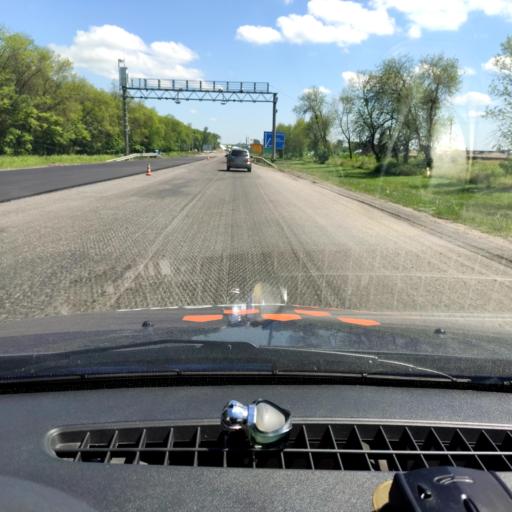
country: RU
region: Orjol
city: Zmiyevka
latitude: 52.7059
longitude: 36.3638
